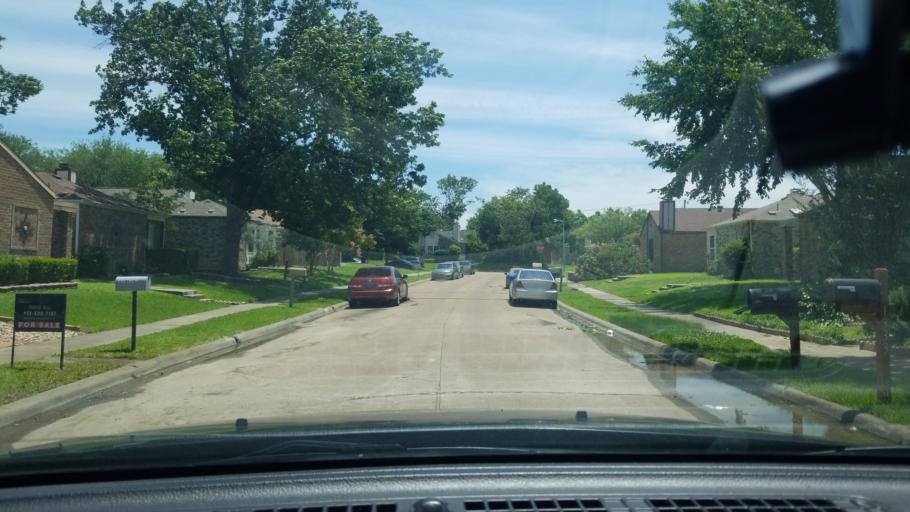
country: US
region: Texas
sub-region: Dallas County
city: Mesquite
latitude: 32.7829
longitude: -96.5998
